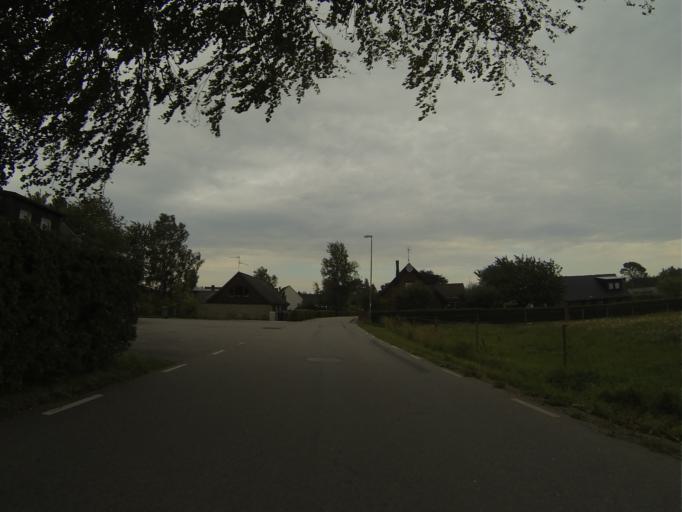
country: SE
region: Skane
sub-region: Staffanstorps Kommun
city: Hjaerup
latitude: 55.6353
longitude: 13.1416
